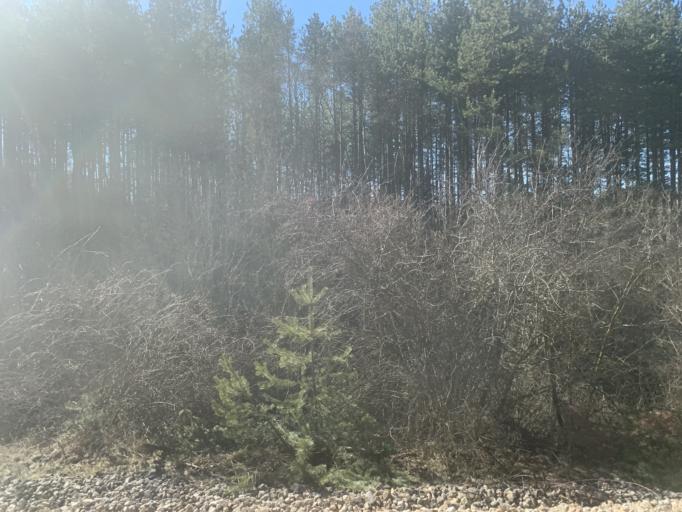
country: BG
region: Sofiya
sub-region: Obshtina Gorna Malina
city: Gorna Malina
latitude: 42.5636
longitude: 23.6877
